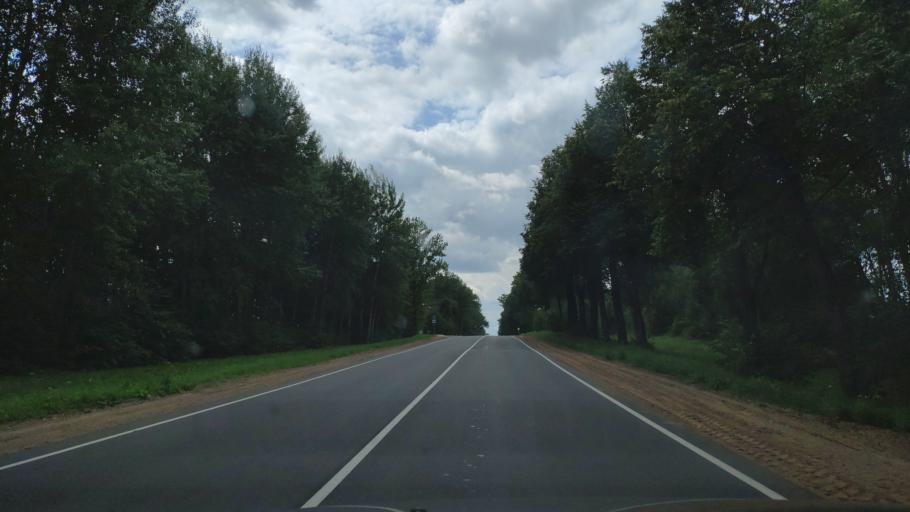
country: BY
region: Minsk
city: Syomkava
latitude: 54.0077
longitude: 27.3783
